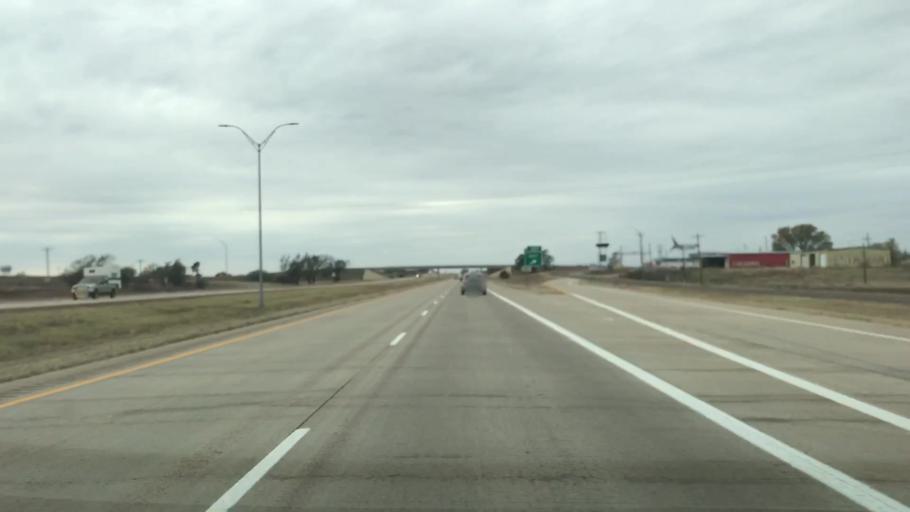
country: US
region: Texas
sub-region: Wheeler County
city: Shamrock
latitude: 35.2270
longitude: -100.1595
